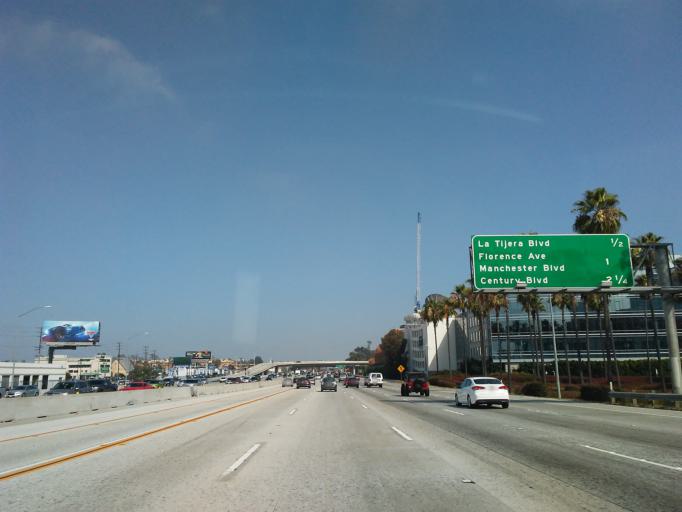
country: US
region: California
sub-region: Los Angeles County
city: Ladera Heights
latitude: 33.9777
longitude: -118.3899
